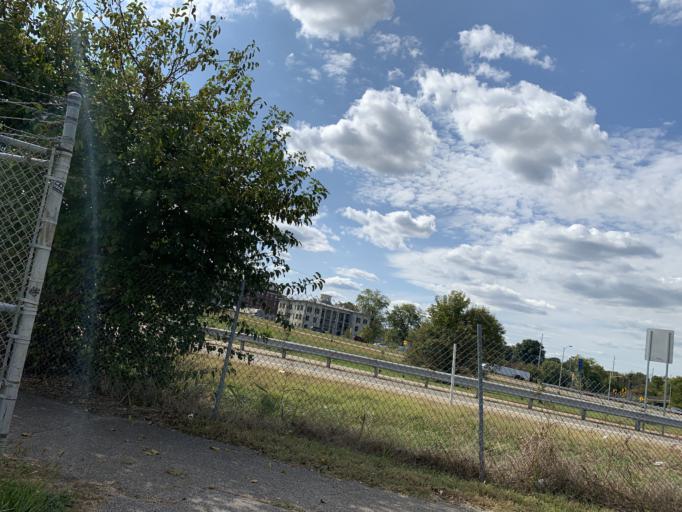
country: US
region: Kentucky
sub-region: Jefferson County
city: Louisville
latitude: 38.2716
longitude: -85.7814
